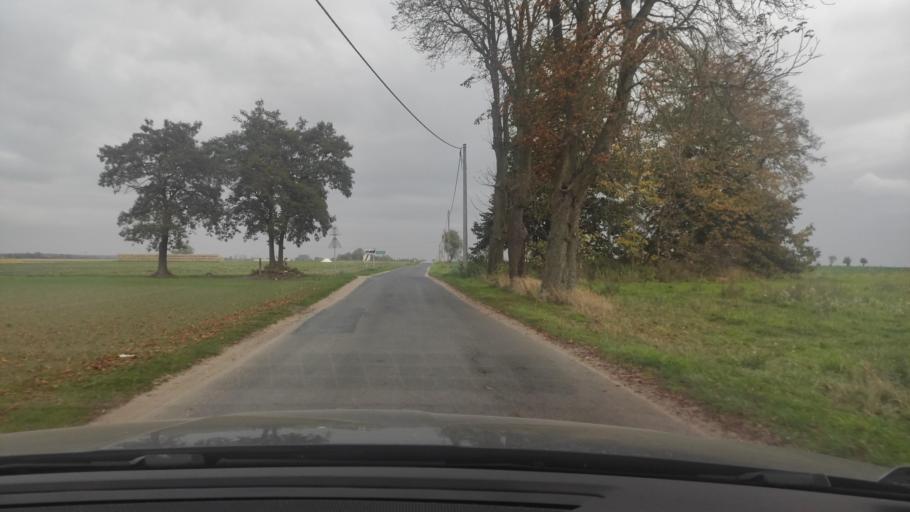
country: PL
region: Greater Poland Voivodeship
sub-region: Powiat poznanski
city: Kostrzyn
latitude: 52.4437
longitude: 17.1737
